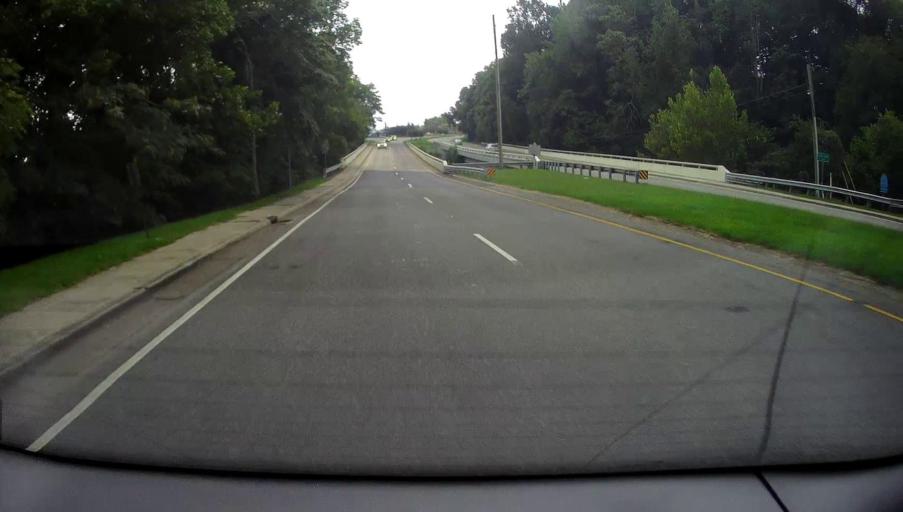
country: US
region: Tennessee
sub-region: Coffee County
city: Manchester
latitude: 35.4872
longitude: -86.0912
